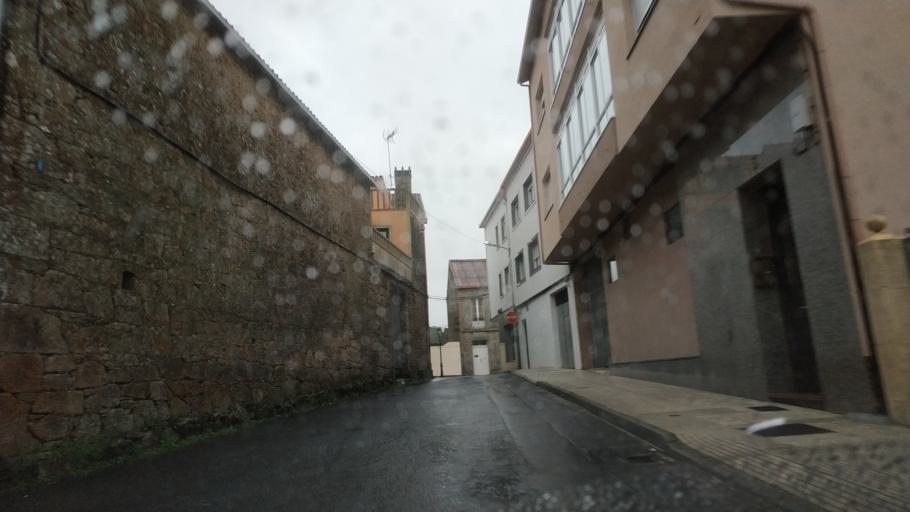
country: ES
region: Galicia
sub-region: Provincia da Coruna
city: Negreira
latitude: 42.9089
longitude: -8.7378
